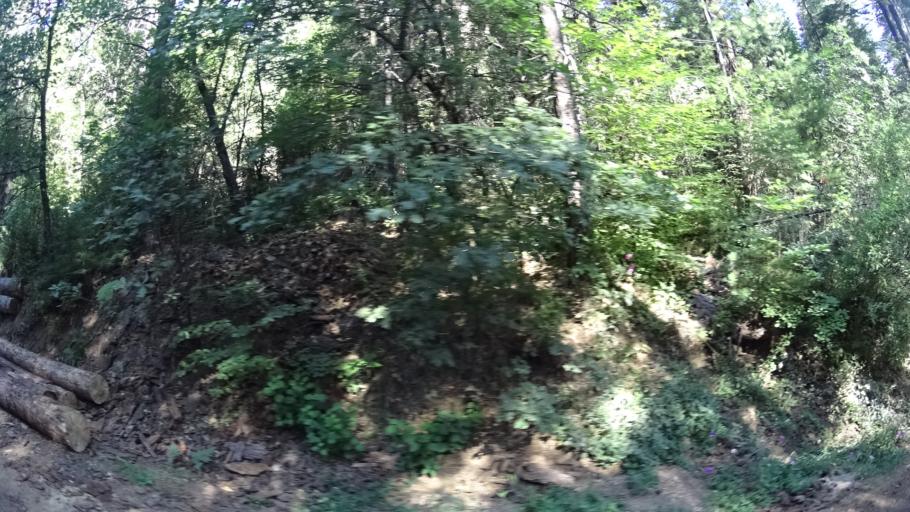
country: US
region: California
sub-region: Calaveras County
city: Arnold
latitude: 38.2610
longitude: -120.3453
